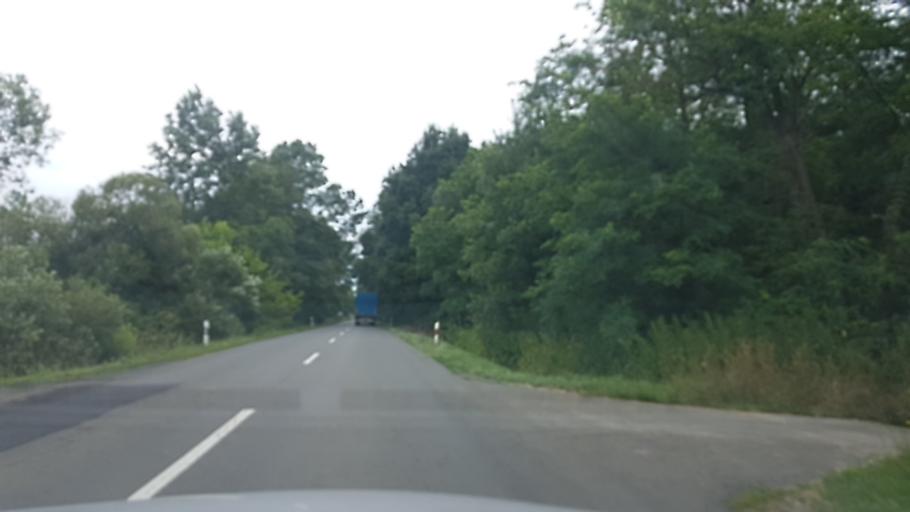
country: HU
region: Baranya
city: Szigetvar
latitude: 46.0257
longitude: 17.6416
